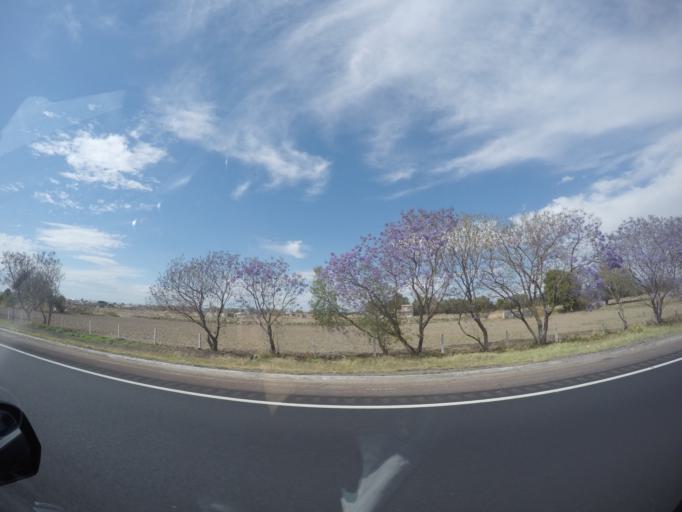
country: MX
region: Guanajuato
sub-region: Celaya
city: La Trinidad
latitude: 20.5542
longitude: -100.7854
